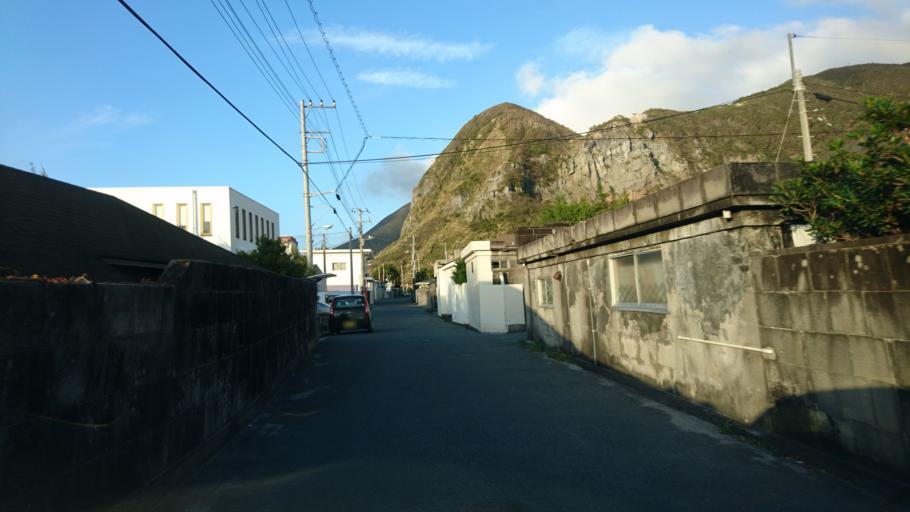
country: JP
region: Shizuoka
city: Shimoda
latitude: 34.3801
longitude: 139.2552
